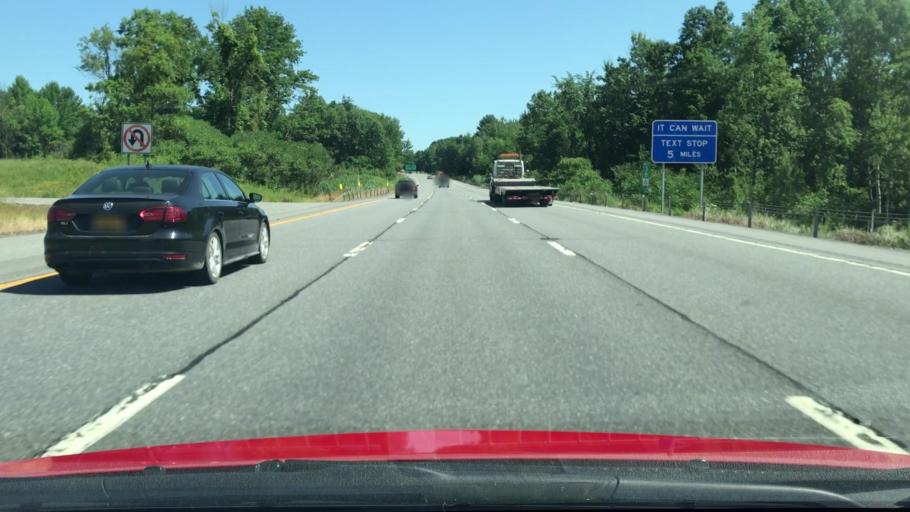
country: US
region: New York
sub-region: Warren County
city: West Glens Falls
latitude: 43.2039
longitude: -73.6957
